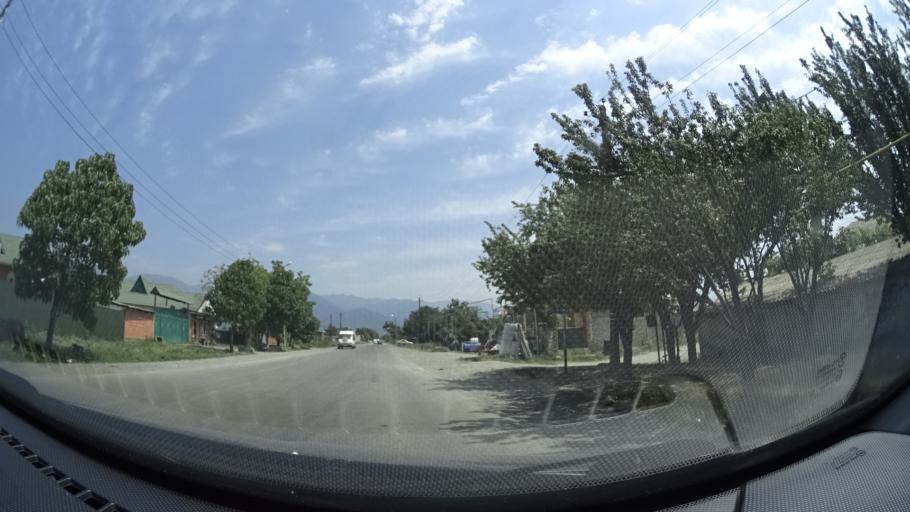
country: GE
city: Bagdadi
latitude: 41.8396
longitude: 46.1107
